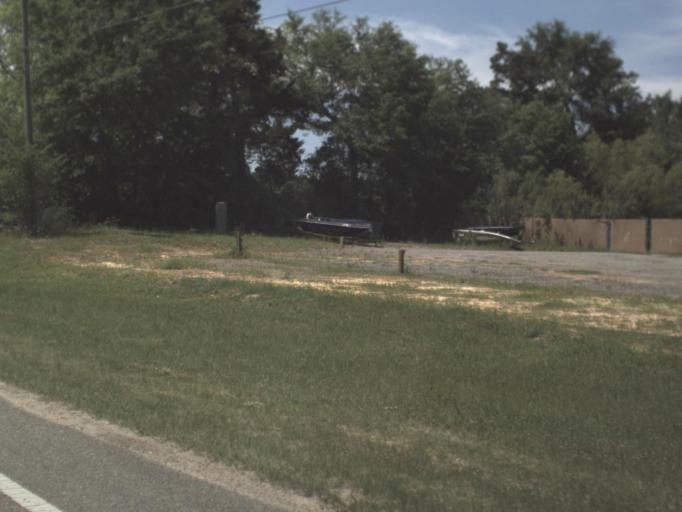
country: US
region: Florida
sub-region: Jackson County
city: Marianna
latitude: 30.7248
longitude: -85.2305
